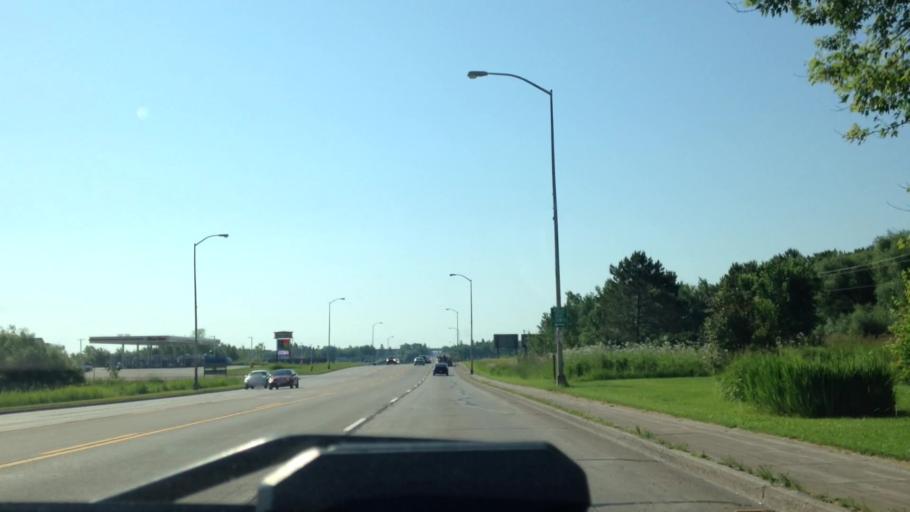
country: US
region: Wisconsin
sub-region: Douglas County
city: Superior
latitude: 46.6991
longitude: -92.0380
